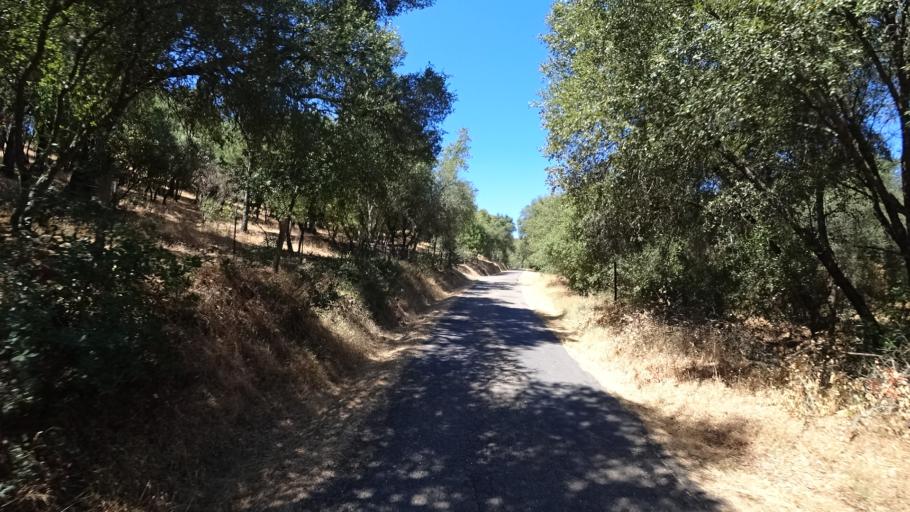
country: US
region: California
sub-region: Calaveras County
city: San Andreas
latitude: 38.2024
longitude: -120.6502
